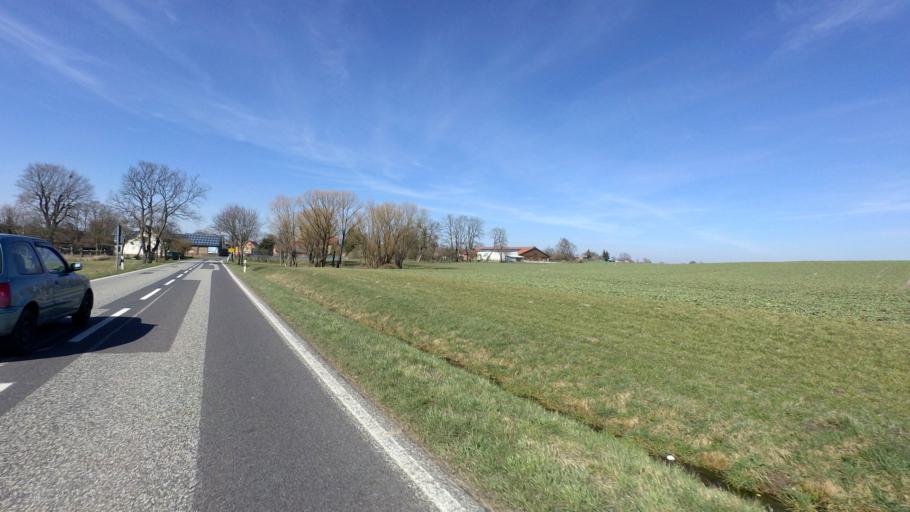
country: DE
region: Brandenburg
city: Furstenwalde
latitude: 52.4275
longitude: 14.0445
